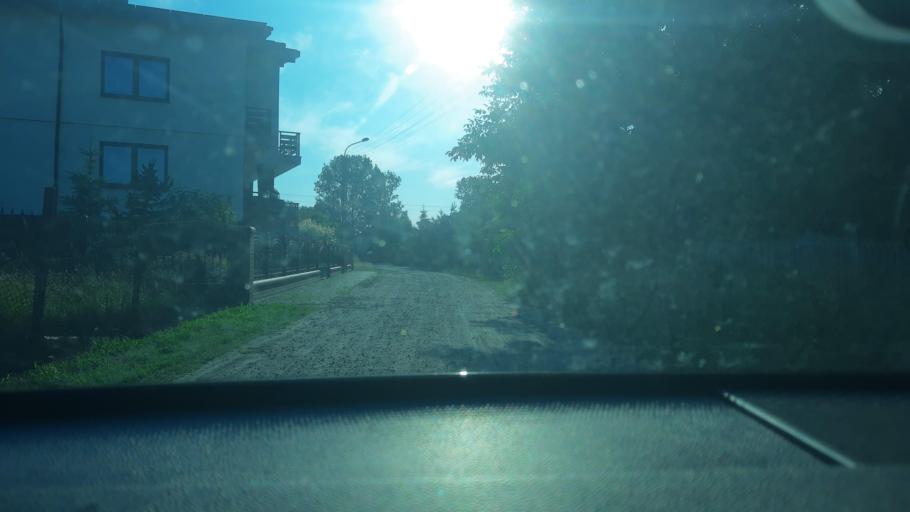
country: PL
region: Lodz Voivodeship
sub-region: Powiat sieradzki
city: Burzenin
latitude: 51.4555
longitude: 18.8438
